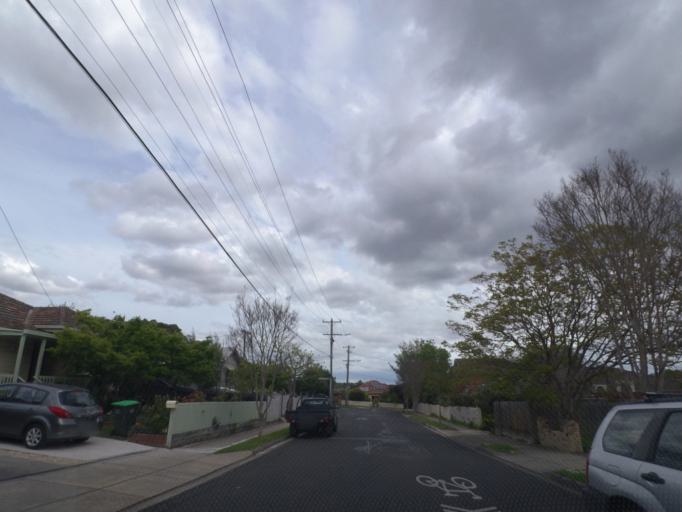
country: AU
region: Victoria
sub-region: Whitehorse
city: Box Hill
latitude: -37.8257
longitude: 145.1284
